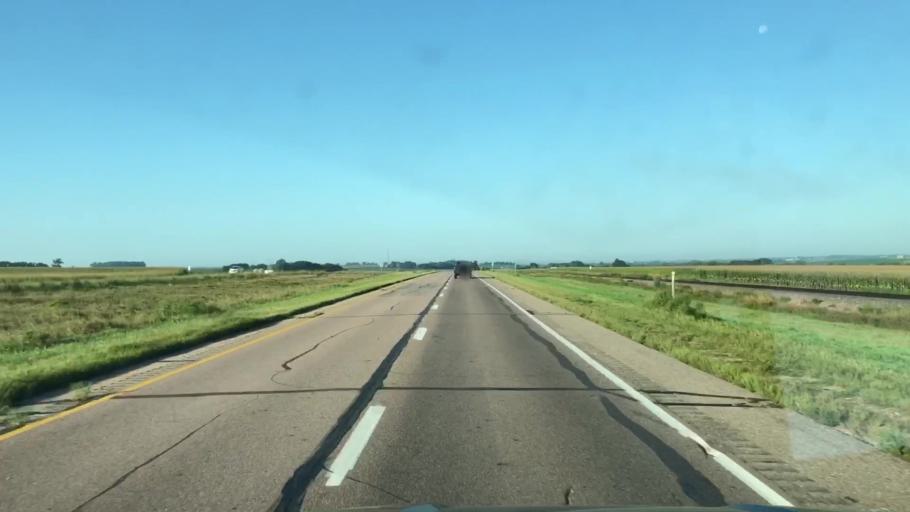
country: US
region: Iowa
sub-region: Sioux County
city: Alton
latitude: 43.0211
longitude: -95.9517
